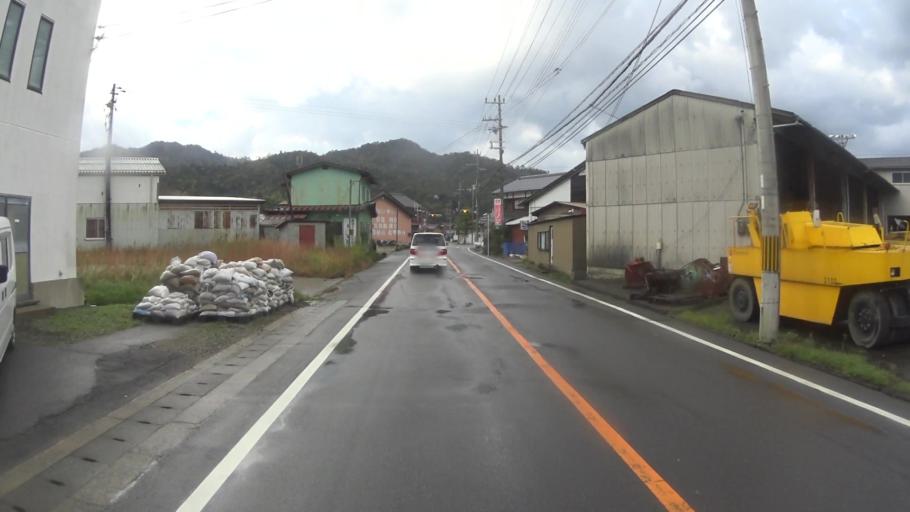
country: JP
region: Kyoto
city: Miyazu
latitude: 35.5509
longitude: 135.1575
